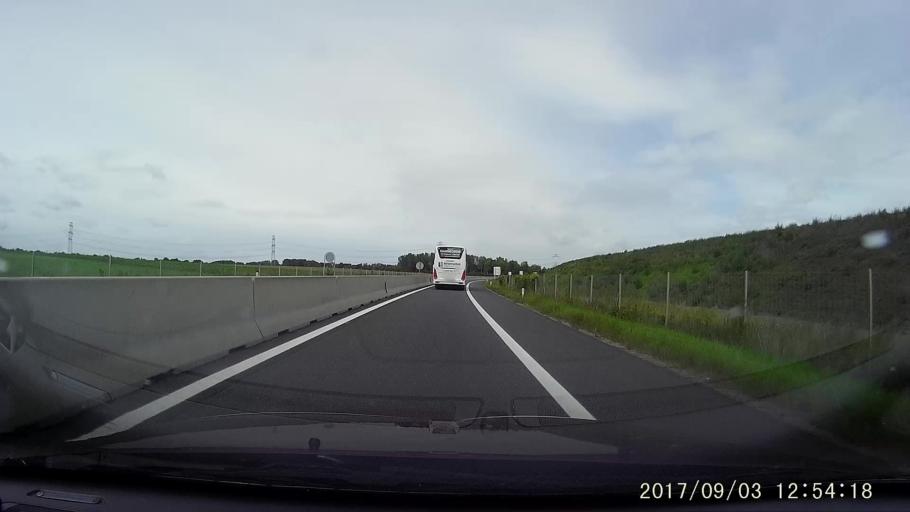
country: AT
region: Lower Austria
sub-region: Politischer Bezirk Korneuburg
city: Sierndorf
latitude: 48.4220
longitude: 16.1592
